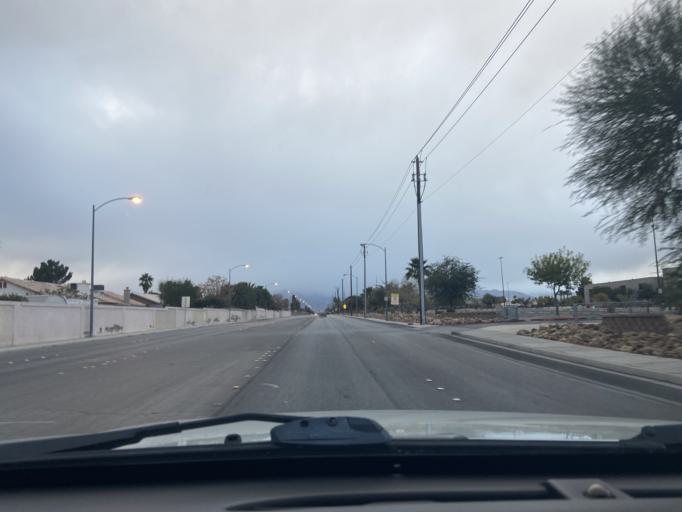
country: US
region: Nevada
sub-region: Clark County
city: North Las Vegas
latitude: 36.2320
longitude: -115.1816
